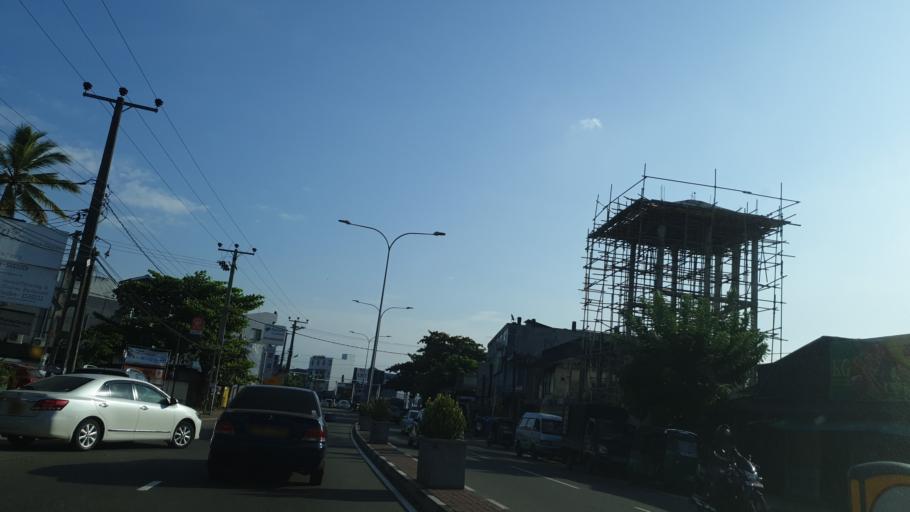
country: LK
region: Western
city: Battaramulla South
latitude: 6.8779
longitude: 79.9352
